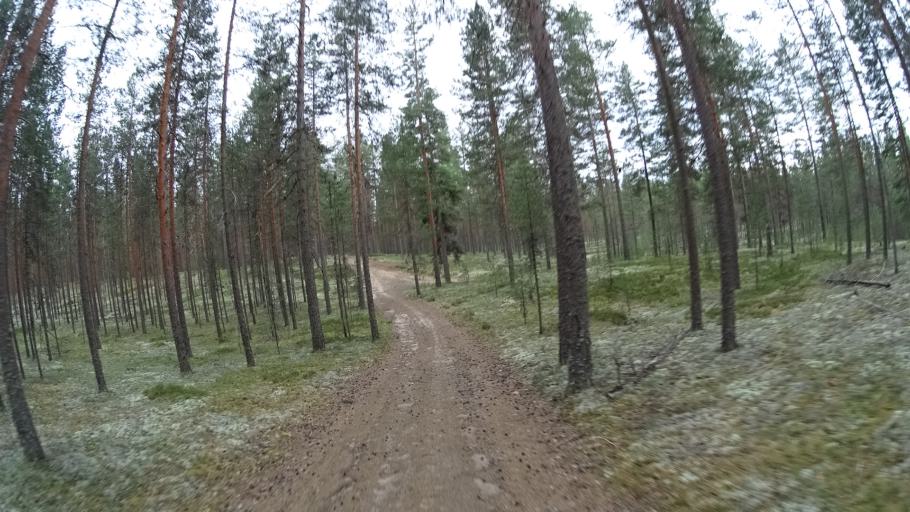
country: FI
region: Satakunta
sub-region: Pohjois-Satakunta
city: Jaemijaervi
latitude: 61.7654
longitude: 22.7499
